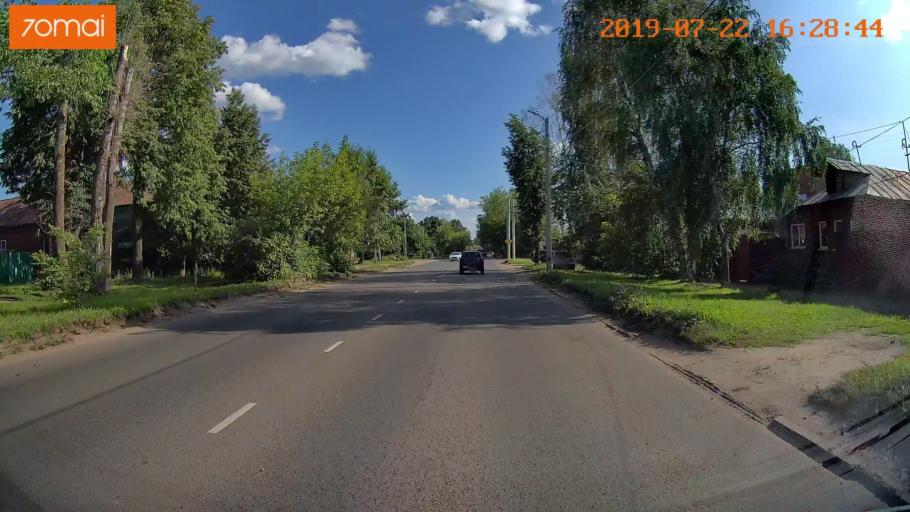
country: RU
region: Ivanovo
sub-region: Gorod Ivanovo
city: Ivanovo
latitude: 57.0370
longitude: 40.9505
